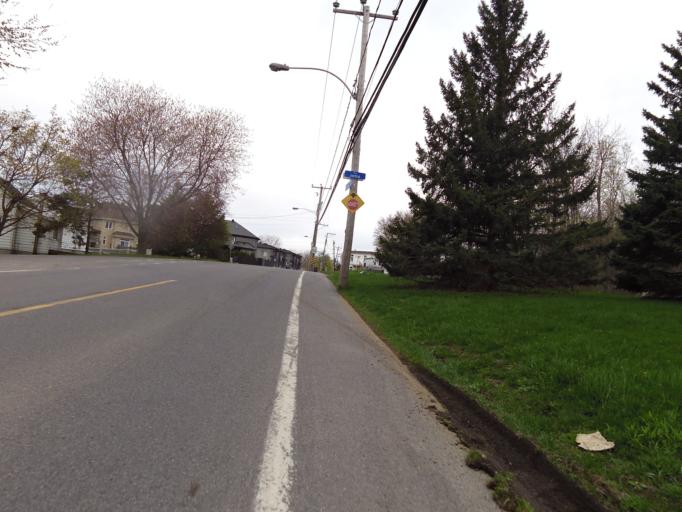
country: CA
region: Quebec
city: Dollard-Des Ormeaux
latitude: 45.5191
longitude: -73.8049
